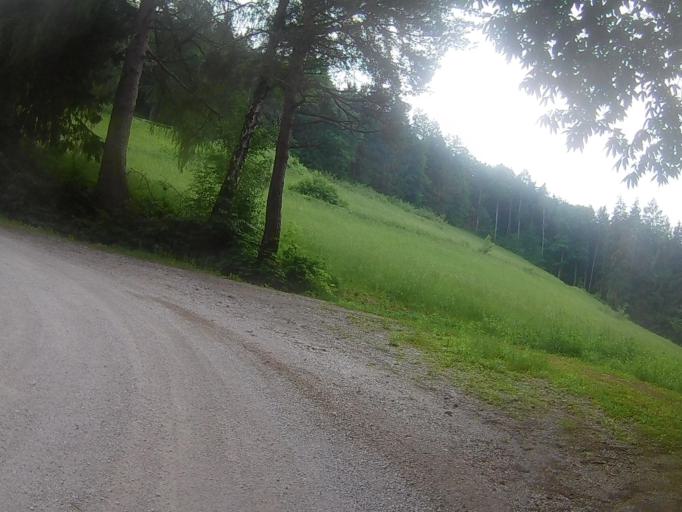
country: SI
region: Ruse
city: Ruse
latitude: 46.5219
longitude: 15.5389
